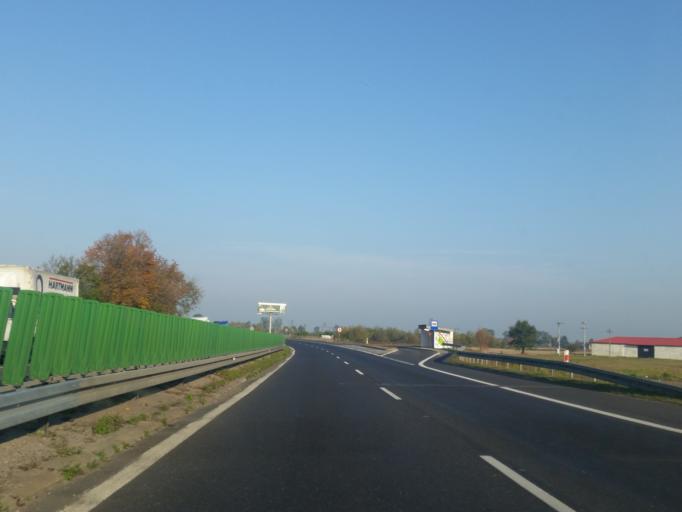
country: PL
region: Masovian Voivodeship
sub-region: Powiat plonski
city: Zaluski
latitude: 52.4768
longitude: 20.5641
